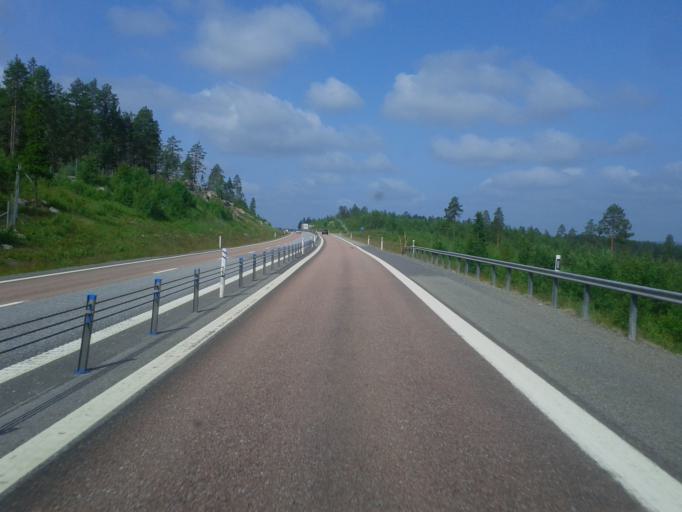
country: SE
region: Vaesterbotten
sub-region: Skelleftea Kommun
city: Soedra Bergsbyn
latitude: 64.6851
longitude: 21.0612
